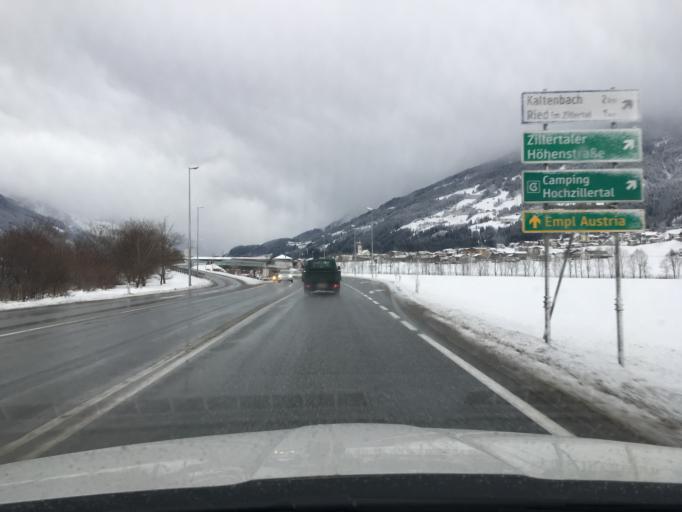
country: AT
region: Tyrol
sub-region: Politischer Bezirk Schwaz
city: Uderns
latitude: 47.3114
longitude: 11.8672
